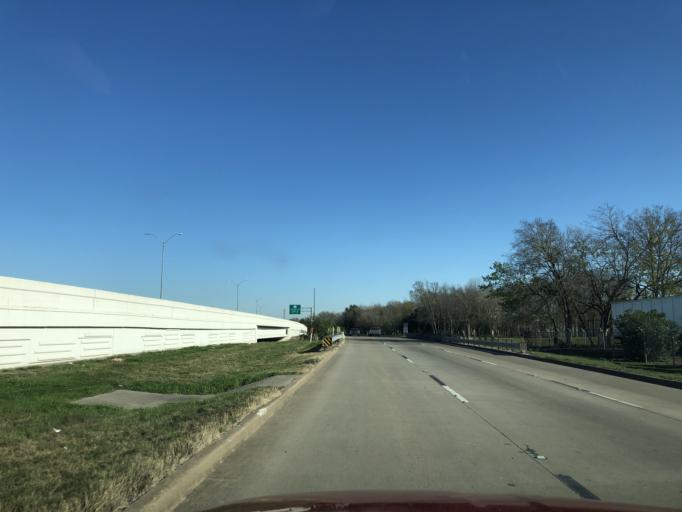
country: US
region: Texas
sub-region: Fort Bend County
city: Fresno
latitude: 29.5969
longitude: -95.4572
